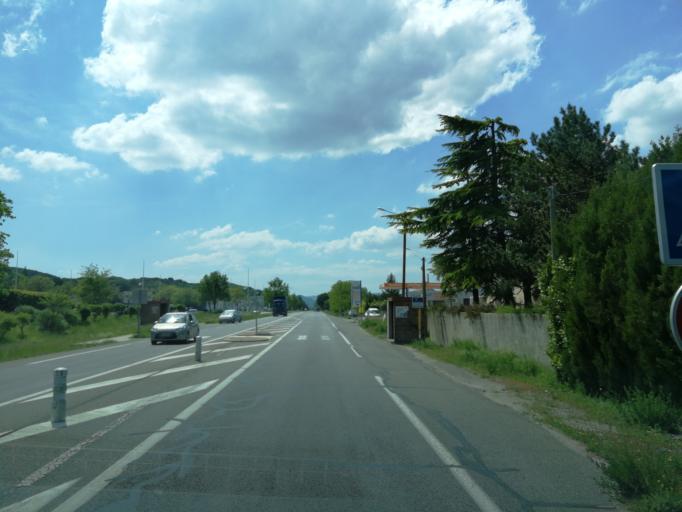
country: FR
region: Rhone-Alpes
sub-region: Departement de la Drome
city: Loriol-sur-Drome
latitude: 44.7605
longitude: 4.8364
